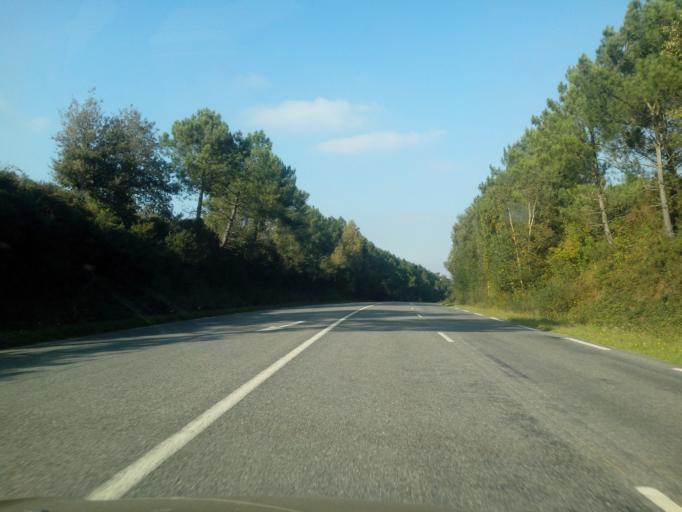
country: FR
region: Brittany
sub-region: Departement du Morbihan
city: Molac
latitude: 47.7069
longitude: -2.4445
